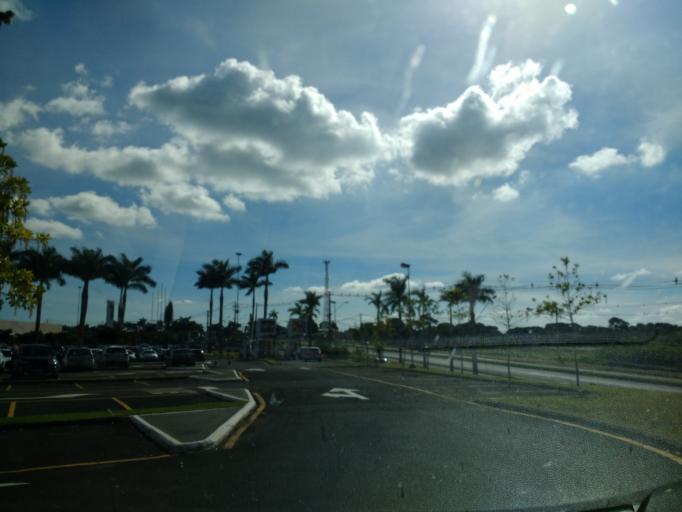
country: BR
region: Parana
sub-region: Maringa
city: Maringa
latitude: -23.4195
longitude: -51.9694
